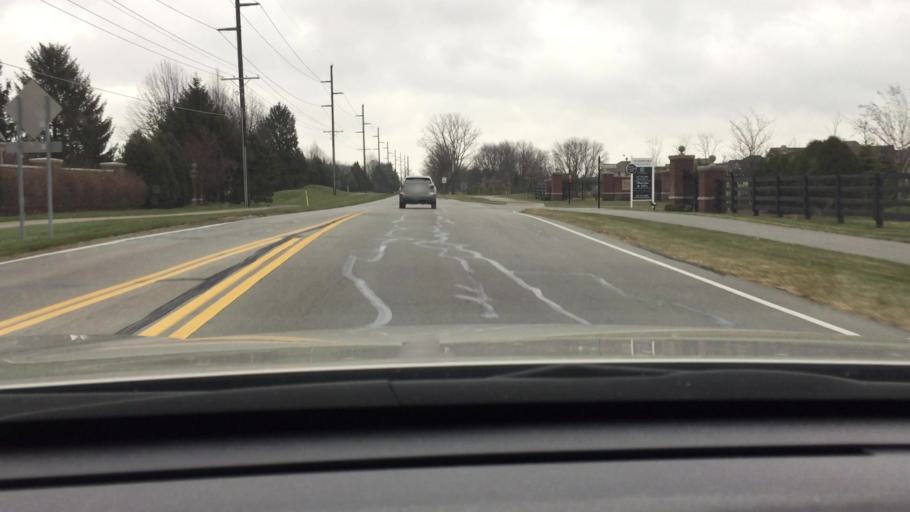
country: US
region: Indiana
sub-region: Hamilton County
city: Carmel
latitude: 40.0076
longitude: -86.1064
